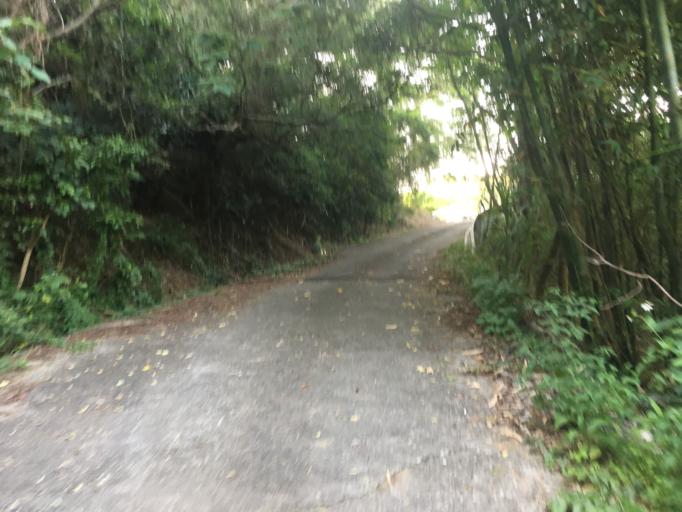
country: TW
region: Taiwan
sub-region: Hsinchu
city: Hsinchu
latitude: 24.7570
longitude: 120.9732
